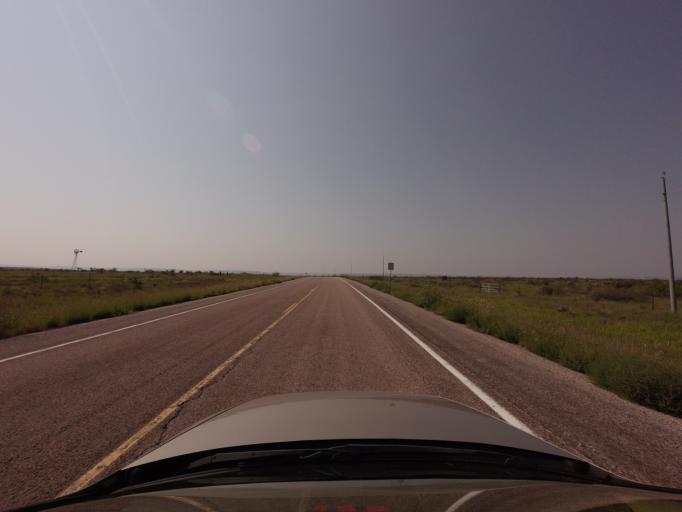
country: US
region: New Mexico
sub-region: Quay County
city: Tucumcari
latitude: 34.9497
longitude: -103.7599
